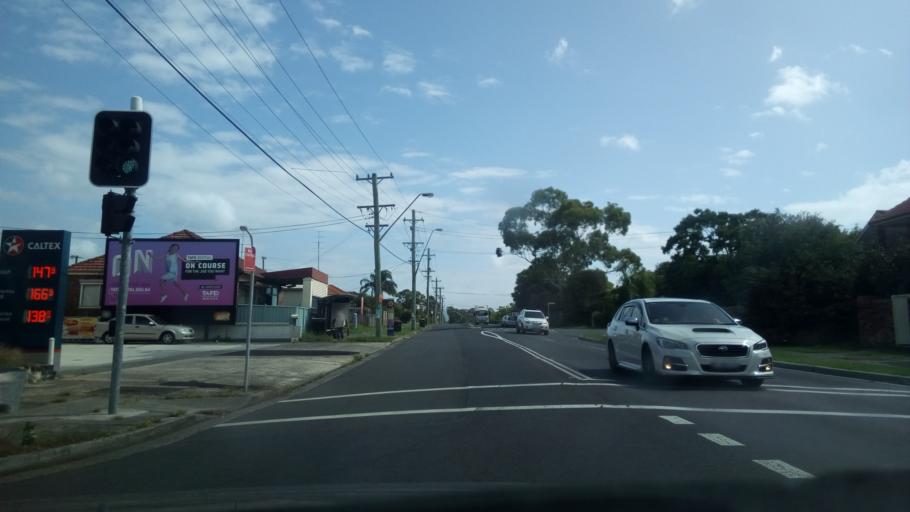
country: AU
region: New South Wales
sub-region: Wollongong
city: Gwynneville
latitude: -34.4164
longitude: 150.8852
